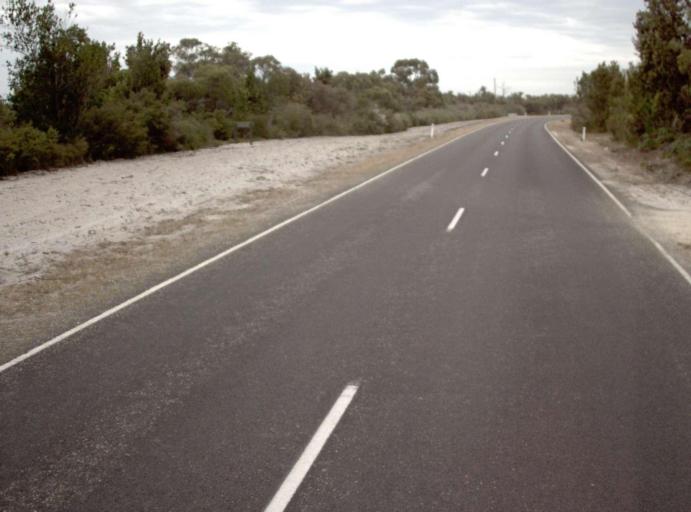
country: AU
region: Victoria
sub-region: Wellington
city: Sale
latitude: -38.1796
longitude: 147.3783
